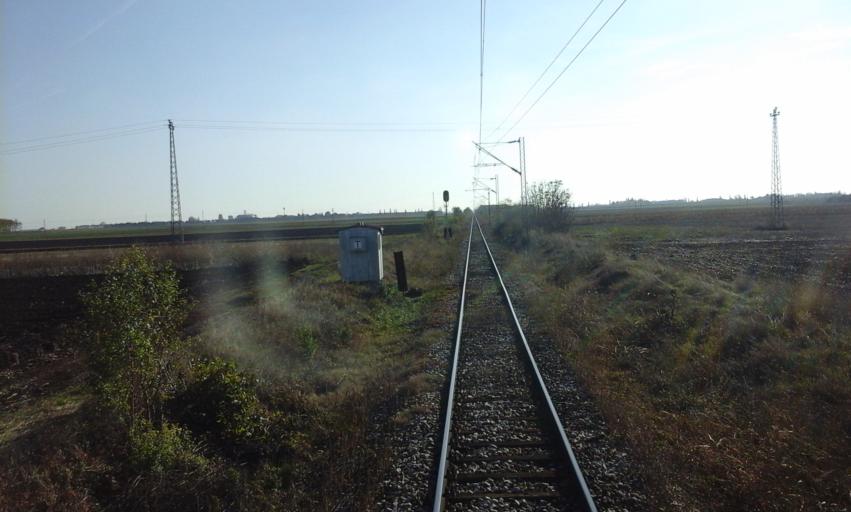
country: RS
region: Autonomna Pokrajina Vojvodina
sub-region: Severnobacki Okrug
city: Backa Topola
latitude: 45.7962
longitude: 19.6473
